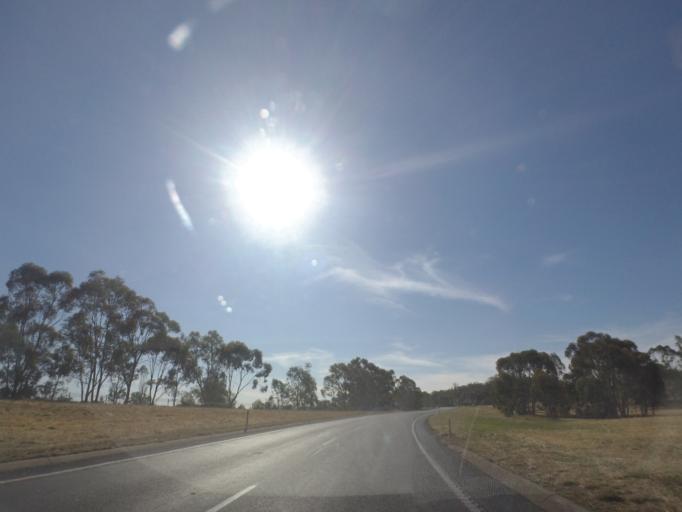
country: AU
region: Victoria
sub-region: Murrindindi
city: Kinglake West
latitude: -36.9852
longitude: 145.1423
